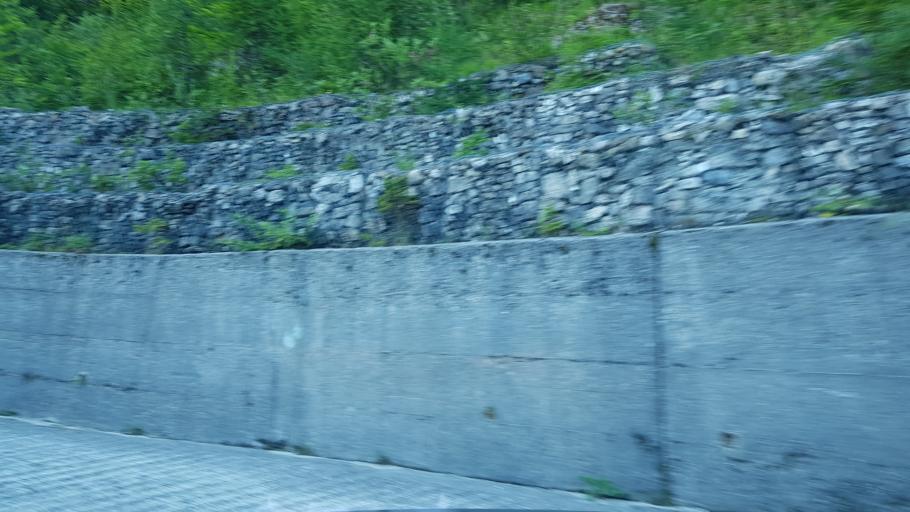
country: IT
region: Friuli Venezia Giulia
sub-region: Provincia di Udine
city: Pontebba
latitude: 46.4805
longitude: 13.2508
